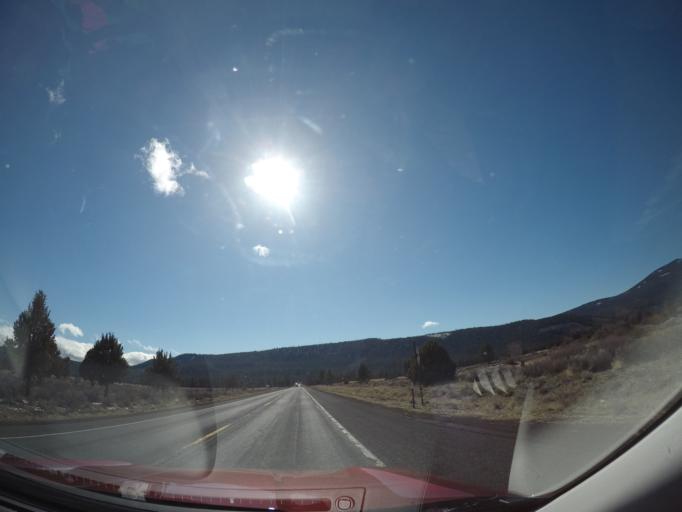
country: US
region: California
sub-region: Siskiyou County
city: Montague
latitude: 41.7665
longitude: -122.0578
